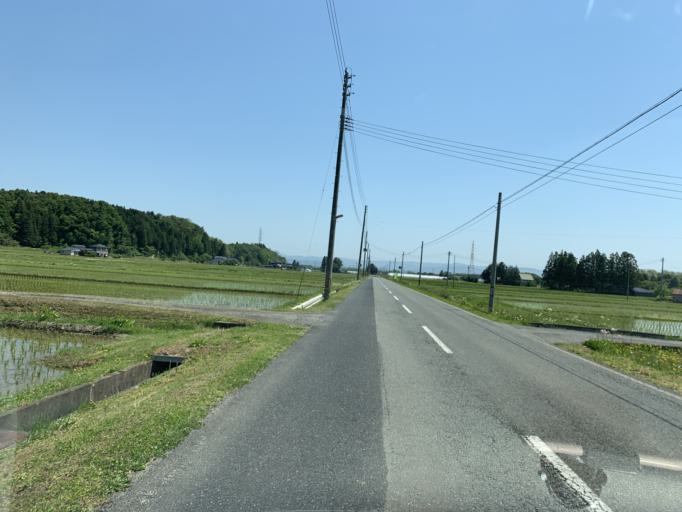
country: JP
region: Iwate
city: Mizusawa
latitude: 39.1599
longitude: 141.0696
